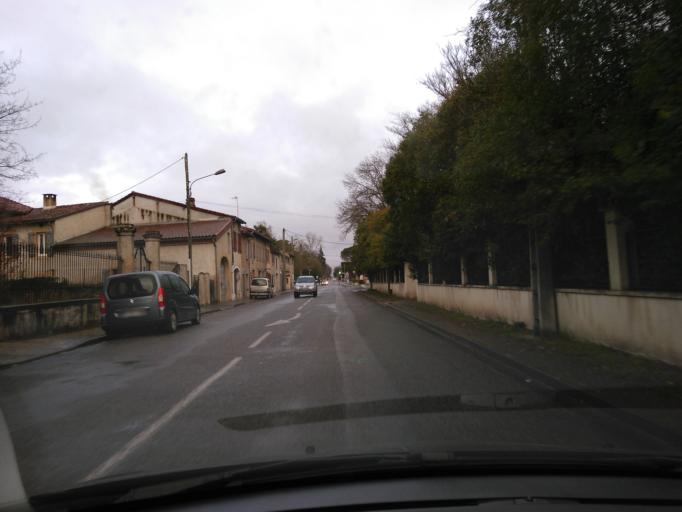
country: FR
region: Midi-Pyrenees
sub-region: Departement de la Haute-Garonne
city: Montesquieu-Volvestre
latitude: 43.1445
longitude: 1.3062
